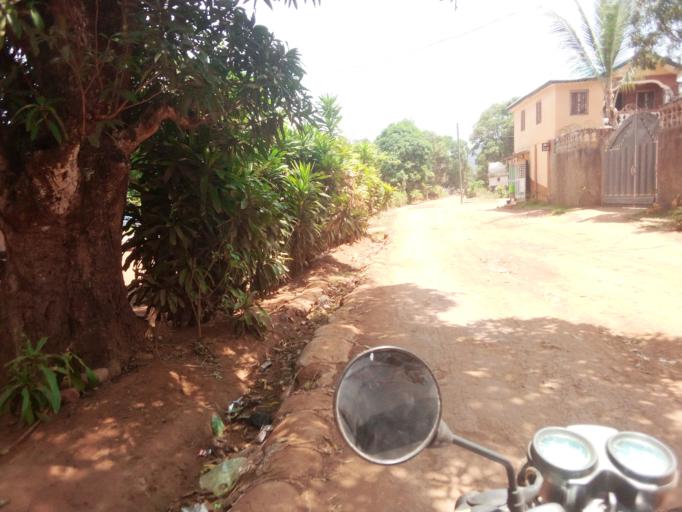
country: SL
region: Western Area
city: Waterloo
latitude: 8.3305
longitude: -13.0785
